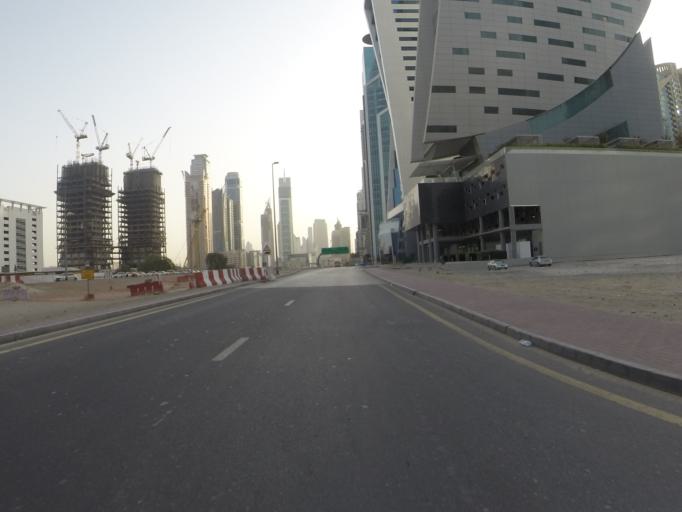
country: AE
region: Dubai
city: Dubai
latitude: 25.1855
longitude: 55.2590
